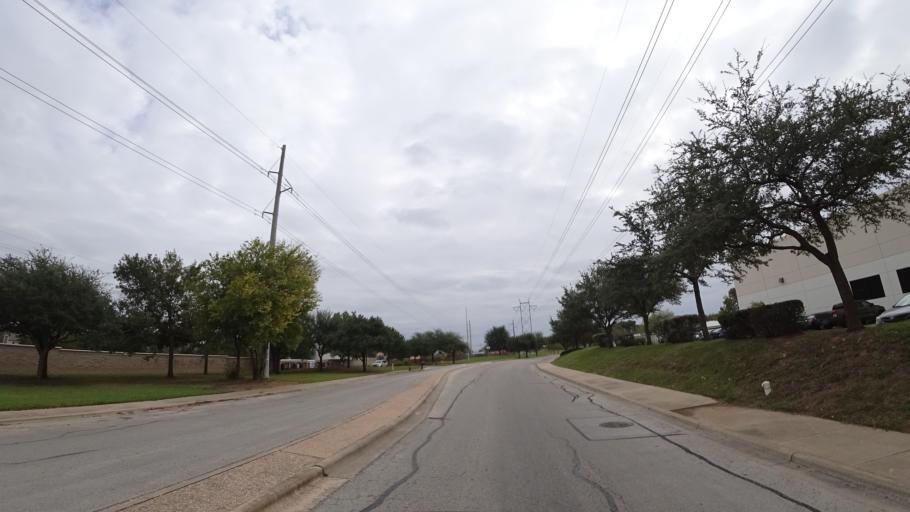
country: US
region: Texas
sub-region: Travis County
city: Wells Branch
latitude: 30.4379
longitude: -97.6882
